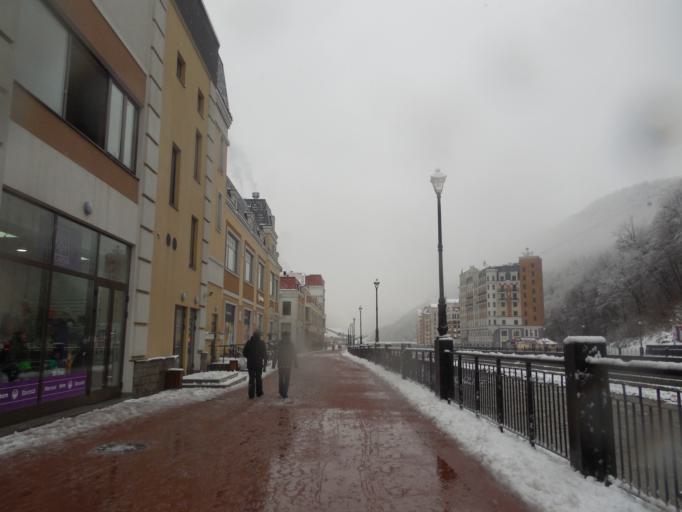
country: RU
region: Krasnodarskiy
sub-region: Sochi City
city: Krasnaya Polyana
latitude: 43.6731
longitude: 40.2908
